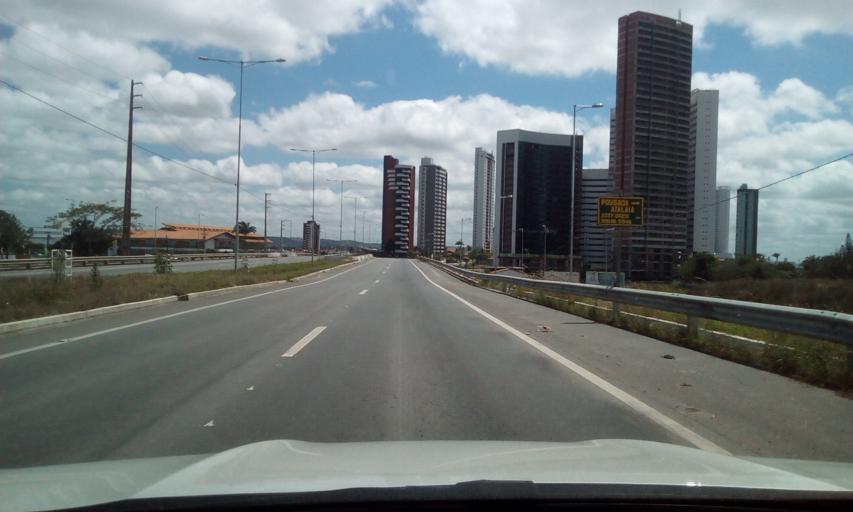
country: BR
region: Paraiba
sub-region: Campina Grande
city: Campina Grande
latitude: -7.2403
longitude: -35.8696
